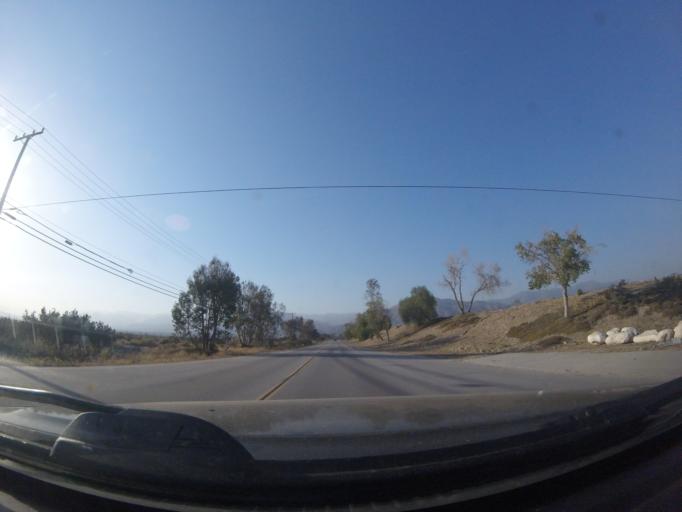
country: US
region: California
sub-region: San Bernardino County
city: Redlands
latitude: 34.0953
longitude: -117.1824
